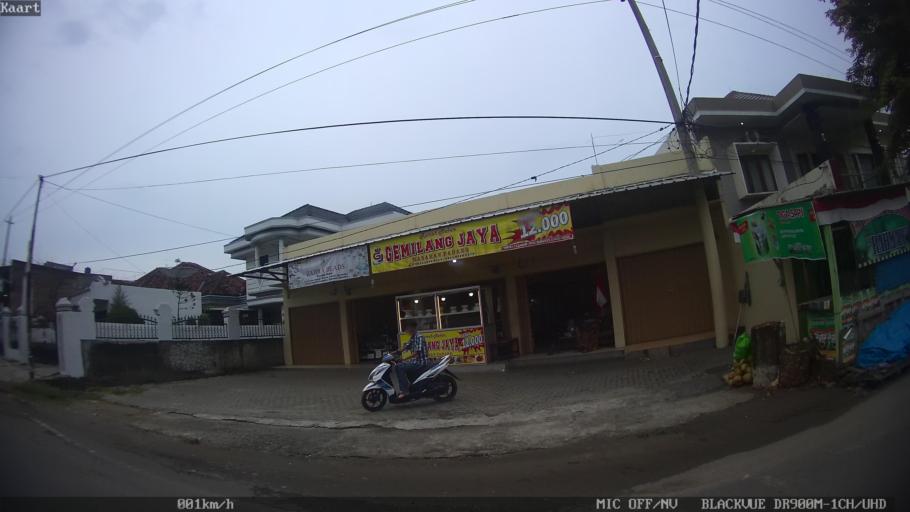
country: ID
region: Lampung
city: Bandarlampung
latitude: -5.4095
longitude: 105.2444
